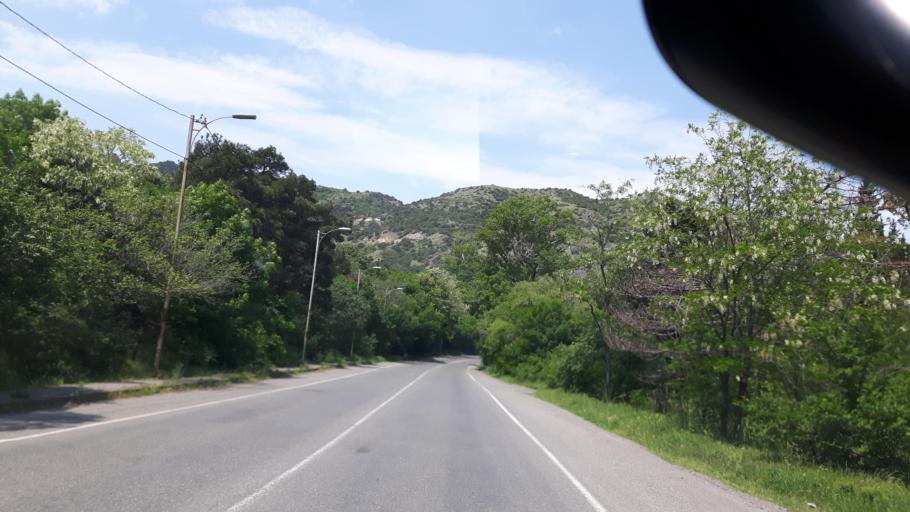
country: GE
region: Mtskheta-Mtianeti
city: Mtskheta
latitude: 41.8303
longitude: 44.7240
